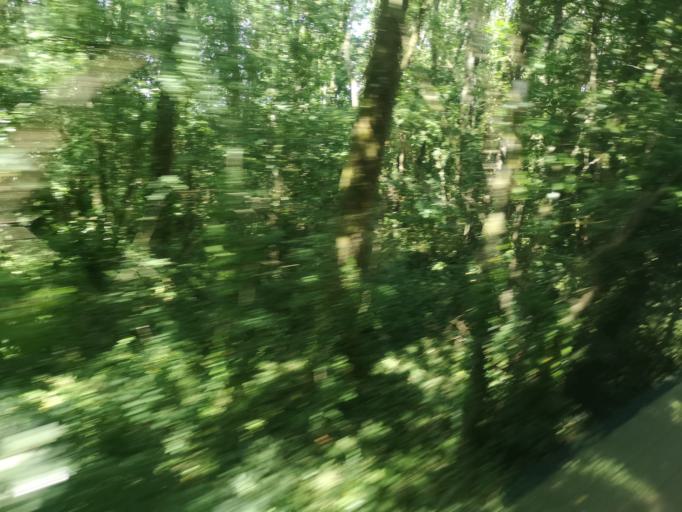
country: GB
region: England
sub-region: Isle of Wight
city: Shalfleet
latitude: 50.6808
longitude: -1.3943
